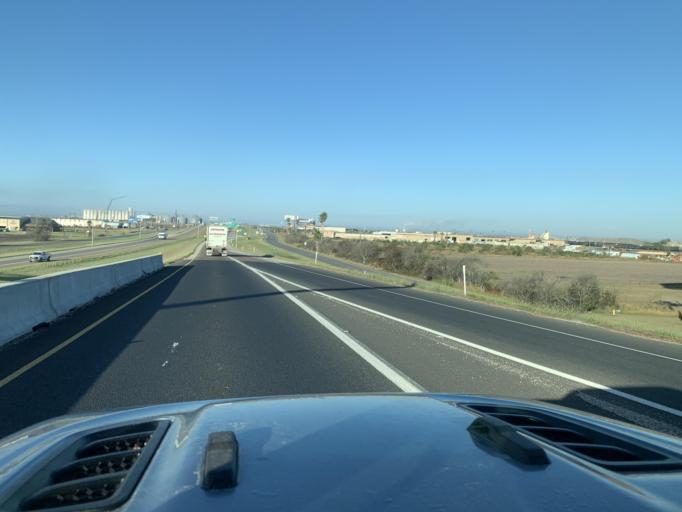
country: US
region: Texas
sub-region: Nueces County
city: Corpus Christi
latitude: 27.7821
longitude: -97.4714
